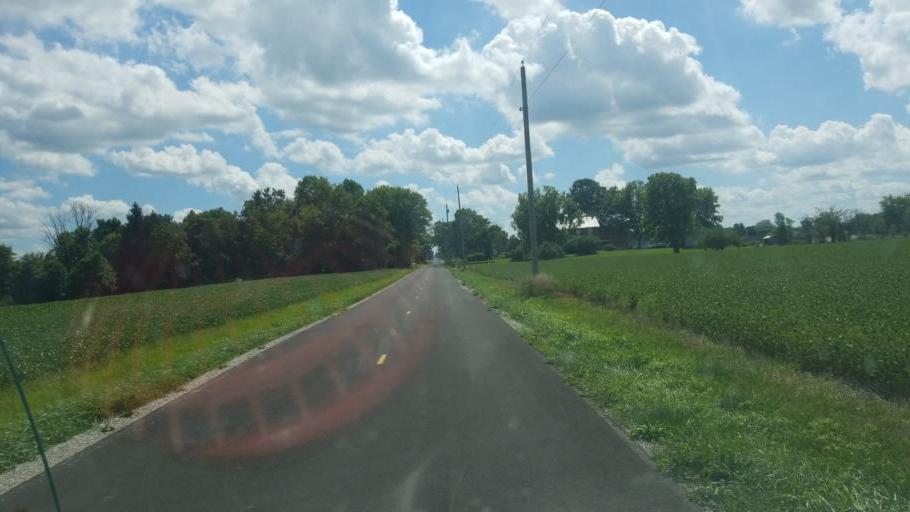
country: US
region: Ohio
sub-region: Marion County
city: Prospect
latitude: 40.4957
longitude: -83.1661
